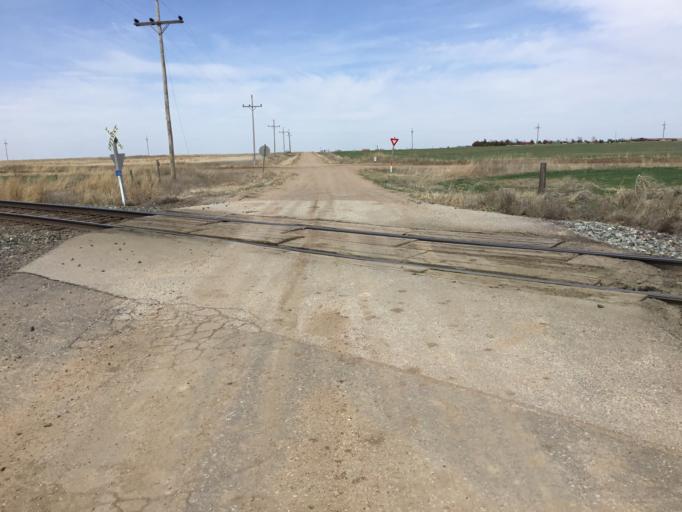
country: US
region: Kansas
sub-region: Trego County
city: WaKeeney
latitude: 39.0270
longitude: -99.9084
